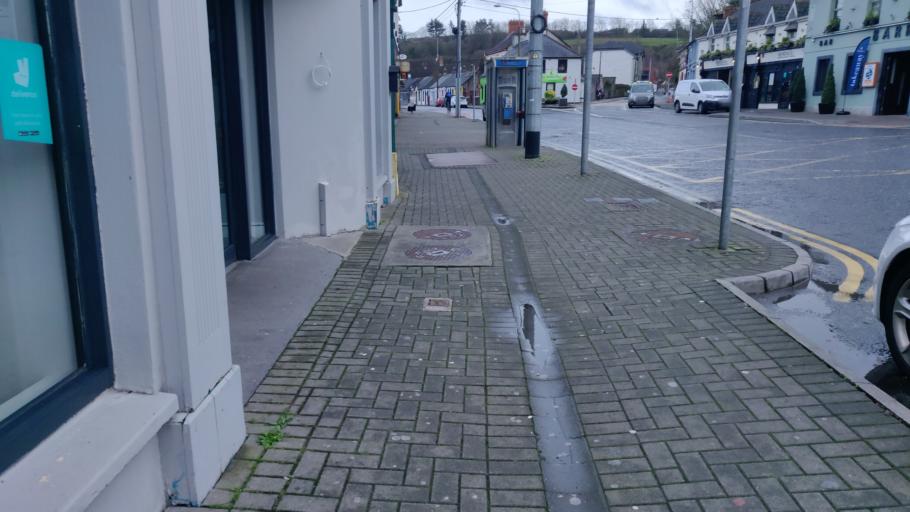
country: IE
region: Munster
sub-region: County Cork
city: Cork
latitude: 51.8775
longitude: -8.4362
